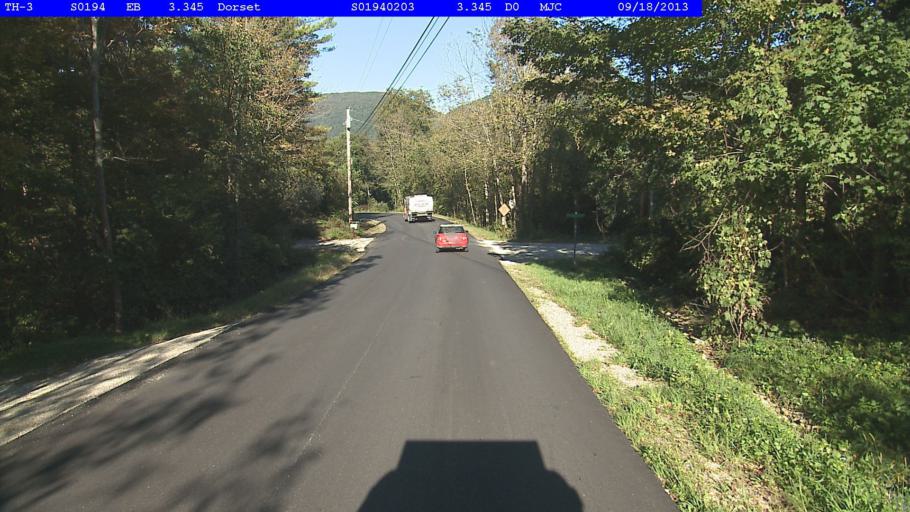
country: US
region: Vermont
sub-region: Bennington County
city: Manchester Center
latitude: 43.2271
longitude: -73.0168
